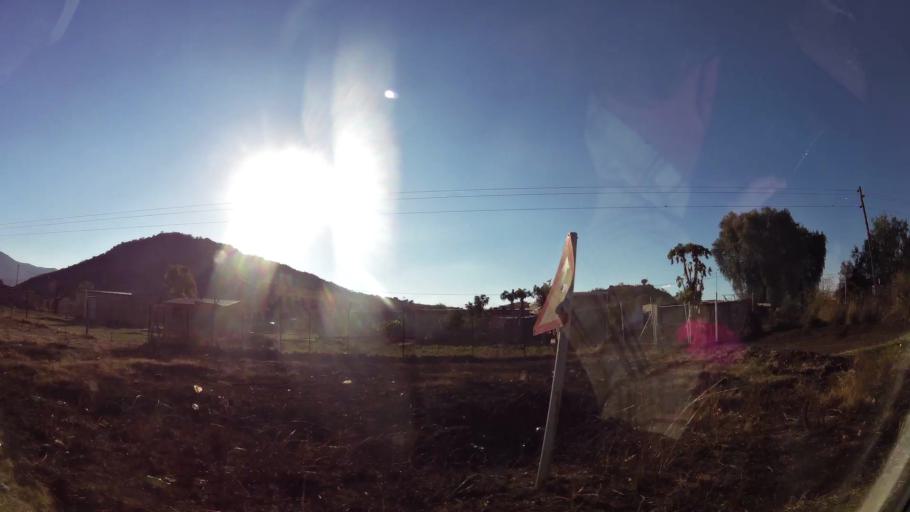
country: ZA
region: Limpopo
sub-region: Waterberg District Municipality
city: Mokopane
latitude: -24.1622
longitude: 28.9788
